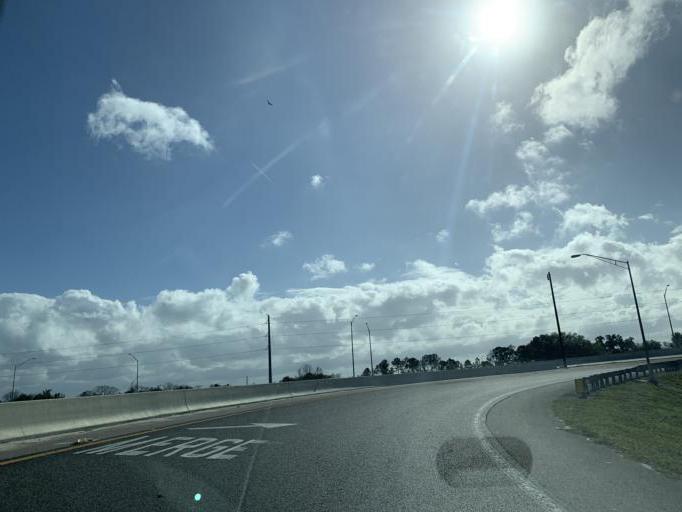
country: US
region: Florida
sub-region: Orange County
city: Lockhart
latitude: 28.6351
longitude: -81.4514
